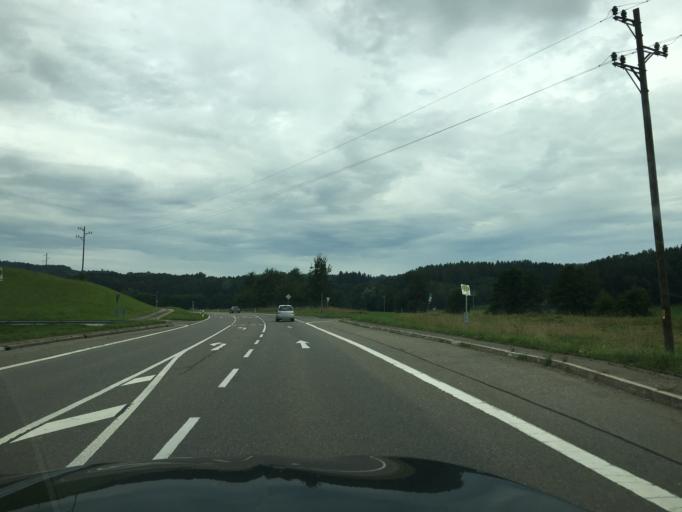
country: DE
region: Baden-Wuerttemberg
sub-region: Freiburg Region
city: Bodman-Ludwigshafen
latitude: 47.8588
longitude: 9.0742
